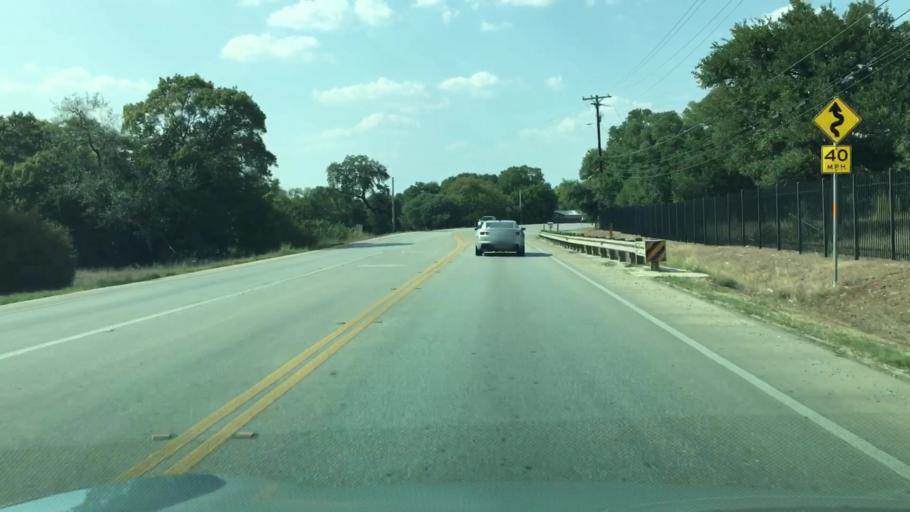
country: US
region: Texas
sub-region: Hays County
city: Dripping Springs
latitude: 30.1860
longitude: -98.0867
